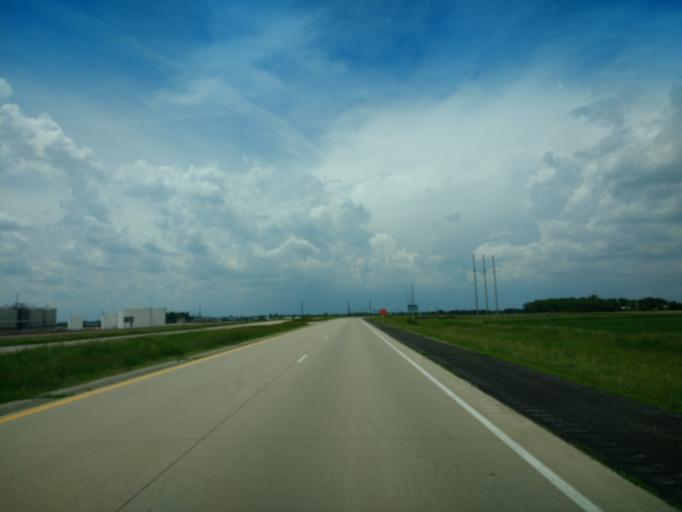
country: US
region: Minnesota
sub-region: Jackson County
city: Lakefield
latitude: 43.8113
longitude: -95.2836
